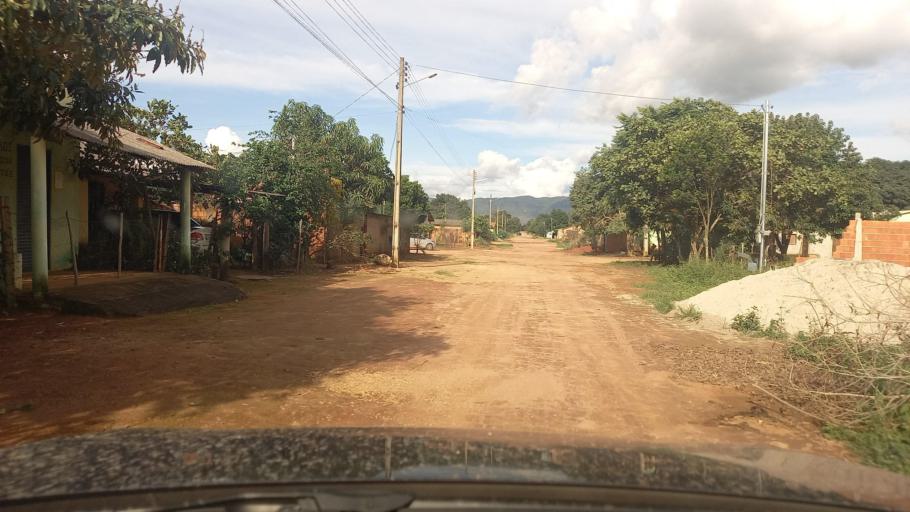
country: BR
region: Goias
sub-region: Cavalcante
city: Cavalcante
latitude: -13.8012
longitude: -47.4452
